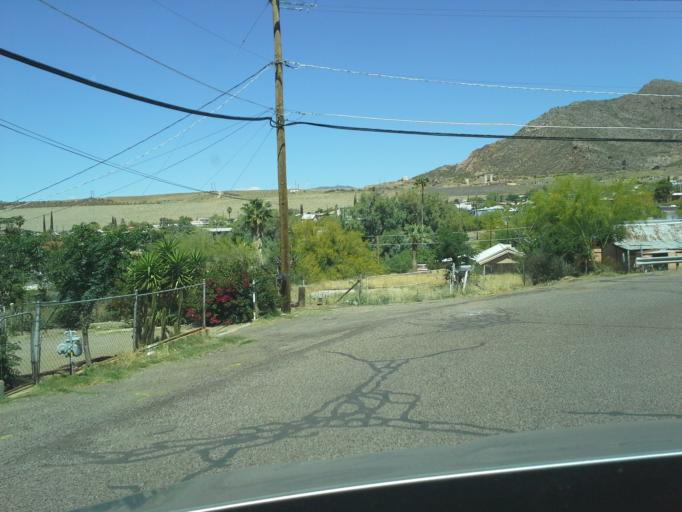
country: US
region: Arizona
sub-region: Pinal County
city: Superior
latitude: 33.2910
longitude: -111.1005
